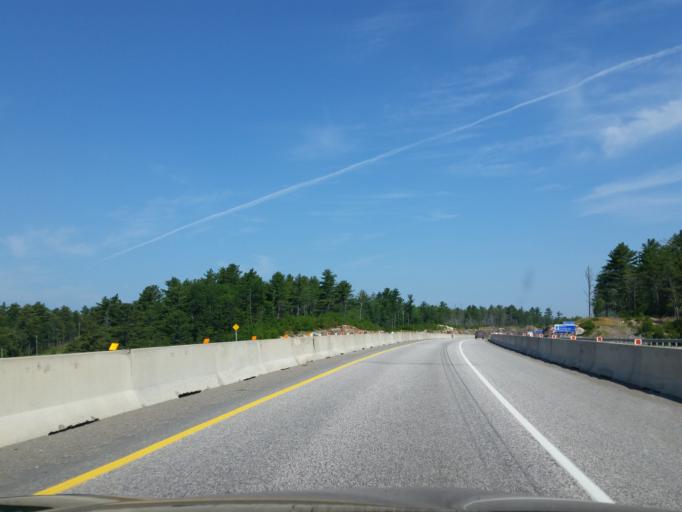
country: CA
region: Ontario
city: Greater Sudbury
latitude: 46.2055
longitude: -80.7641
